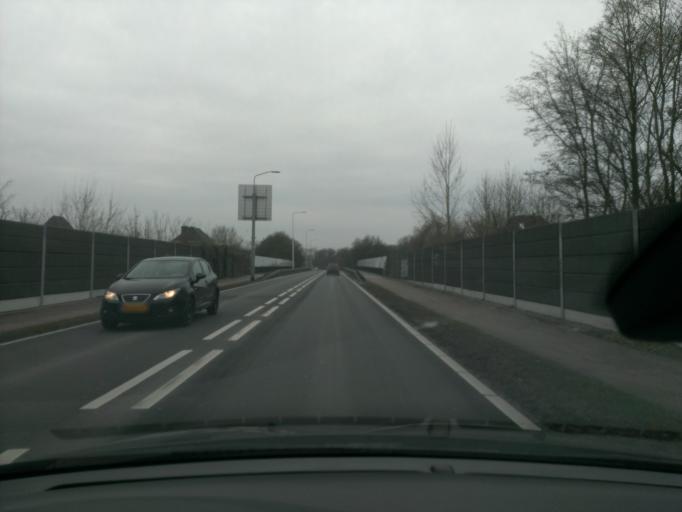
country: NL
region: Overijssel
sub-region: Gemeente Almelo
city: Almelo
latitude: 52.3633
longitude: 6.6723
